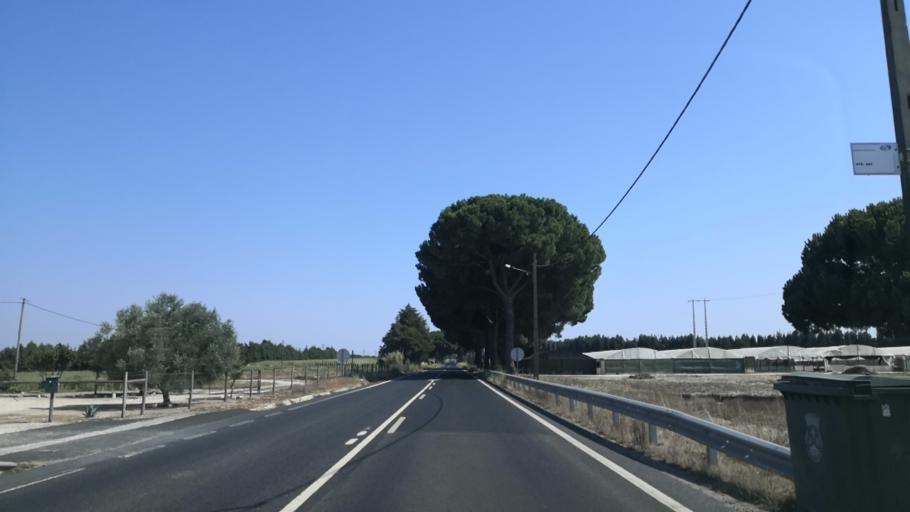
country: PT
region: Santarem
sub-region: Benavente
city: Poceirao
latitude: 38.7332
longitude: -8.6505
